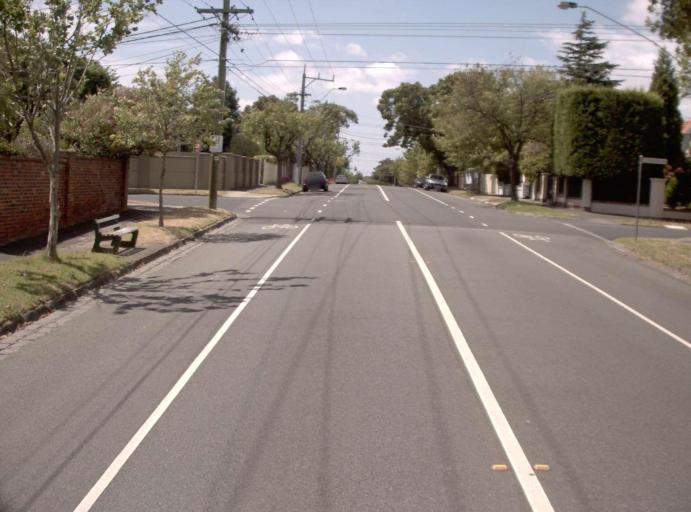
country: AU
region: Victoria
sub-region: Bayside
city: North Brighton
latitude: -37.9168
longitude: 145.0064
